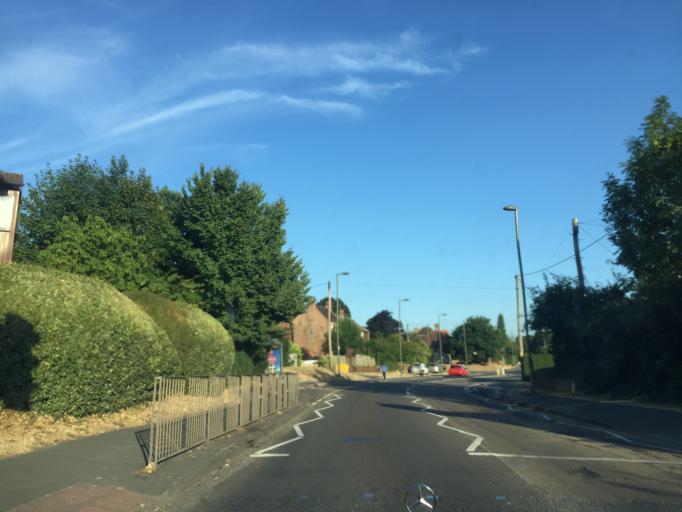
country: GB
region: England
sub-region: Surrey
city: Frimley
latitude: 51.3143
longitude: -0.7387
